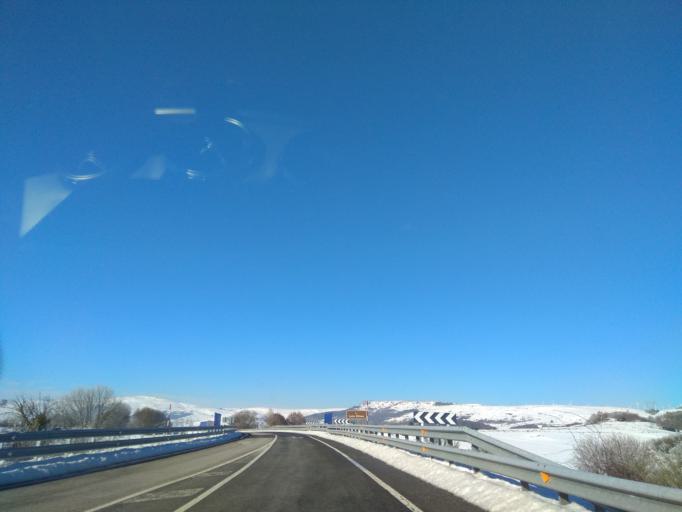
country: ES
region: Castille and Leon
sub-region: Provincia de Burgos
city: Arija
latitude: 43.0067
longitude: -3.8427
